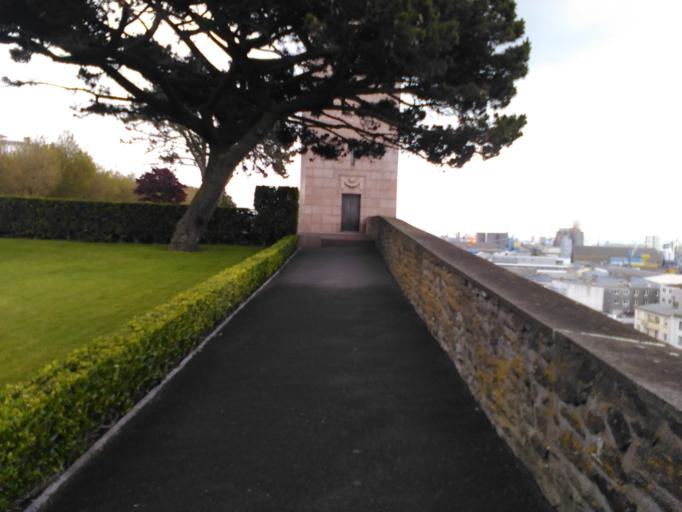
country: FR
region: Brittany
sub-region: Departement du Finistere
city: Brest
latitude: 48.3834
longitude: -4.4869
